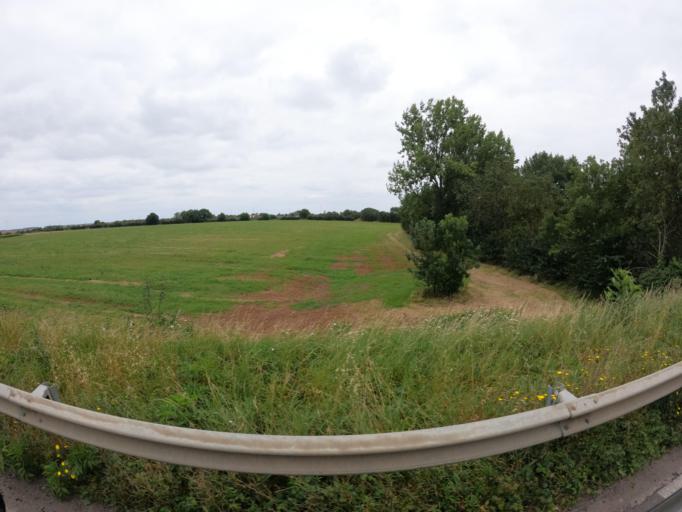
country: FR
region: Pays de la Loire
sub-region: Departement de la Vendee
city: Maillezais
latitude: 46.4121
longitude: -0.6905
